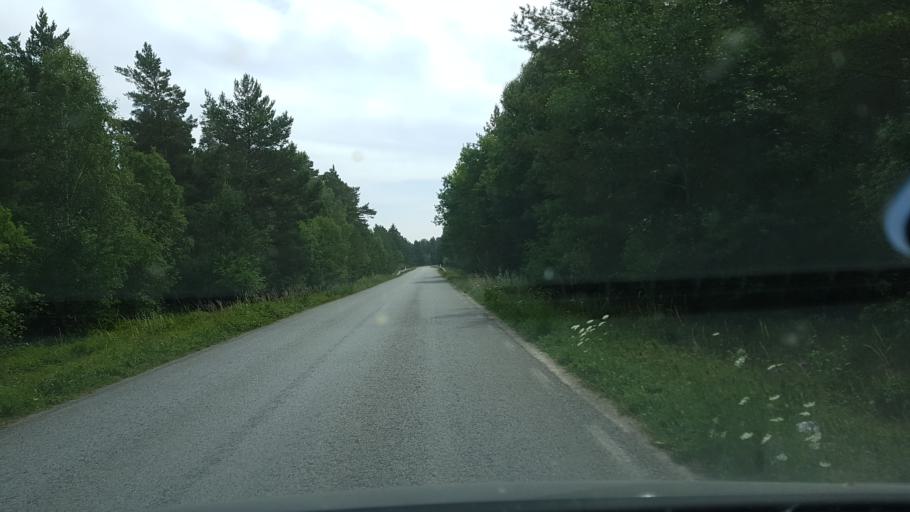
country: SE
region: Gotland
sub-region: Gotland
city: Visby
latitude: 57.7212
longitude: 18.5087
